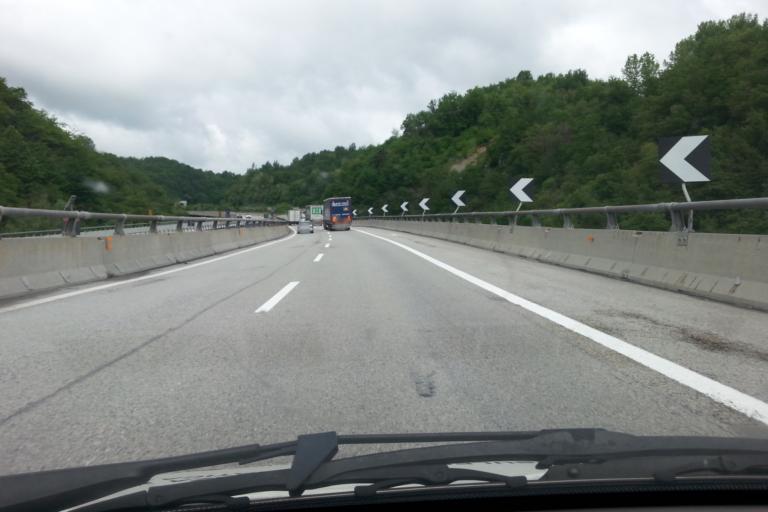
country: IT
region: Liguria
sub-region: Provincia di Savona
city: Valzemola
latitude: 44.3589
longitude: 8.1669
